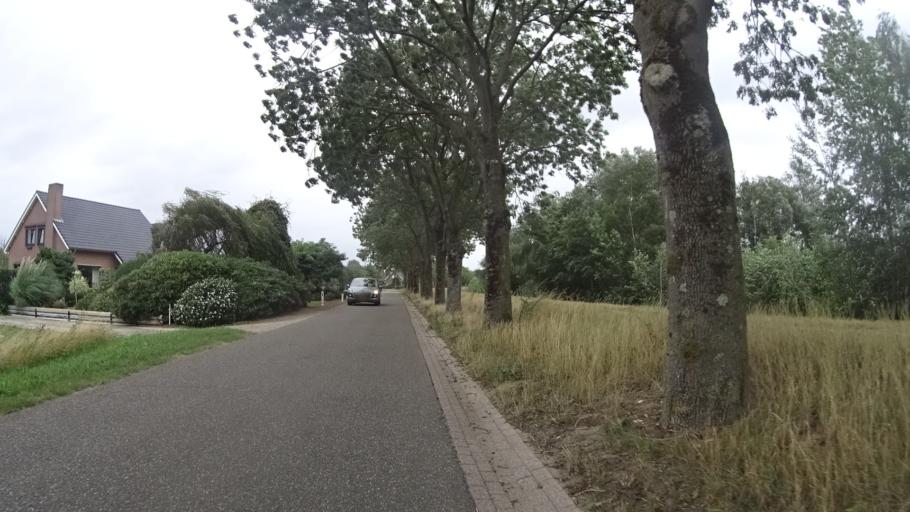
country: NL
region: Limburg
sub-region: Gemeente Venlo
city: Tegelen
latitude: 51.3492
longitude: 6.1291
